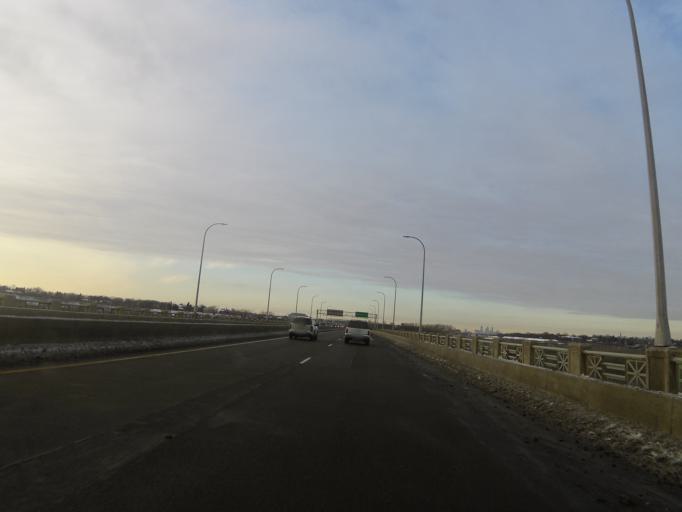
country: US
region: Minnesota
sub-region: Dakota County
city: Mendota Heights
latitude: 44.8851
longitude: -93.1738
